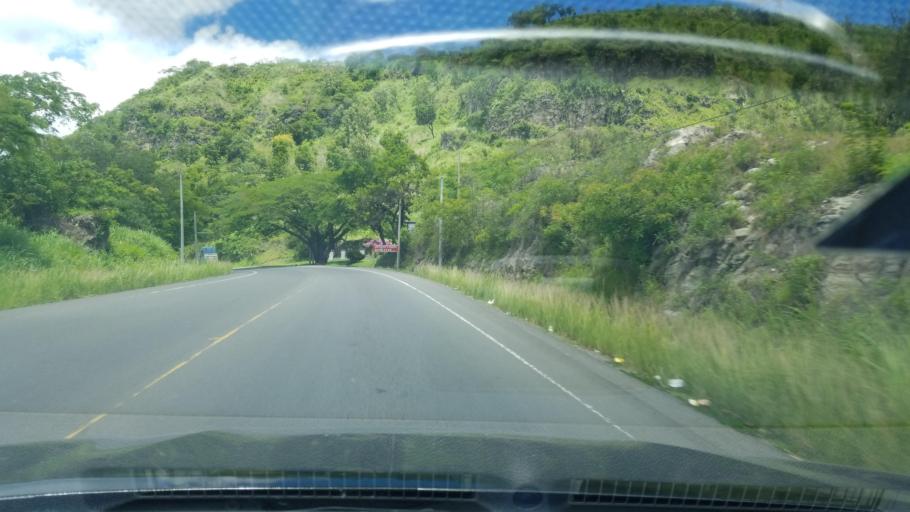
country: HN
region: Francisco Morazan
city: Rio Abajo
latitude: 14.1954
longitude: -87.2064
